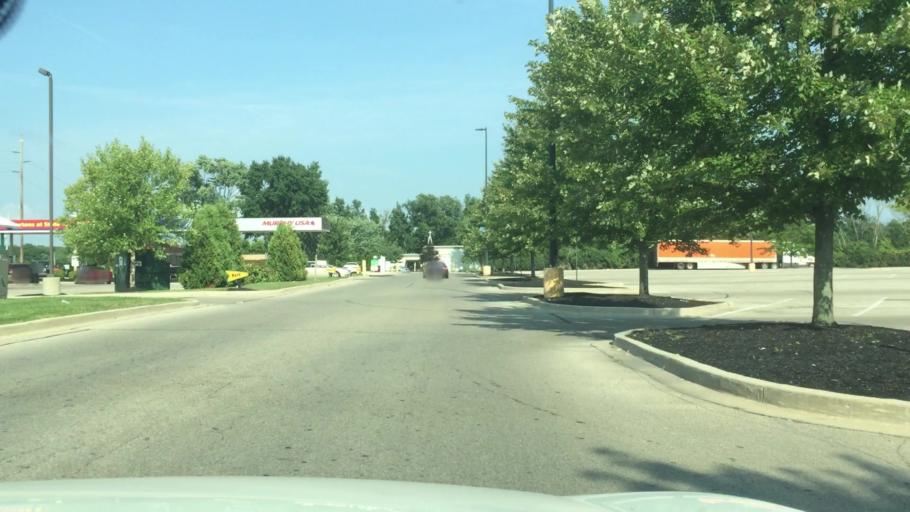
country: US
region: Ohio
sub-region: Clark County
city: Springfield
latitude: 39.9224
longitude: -83.7466
